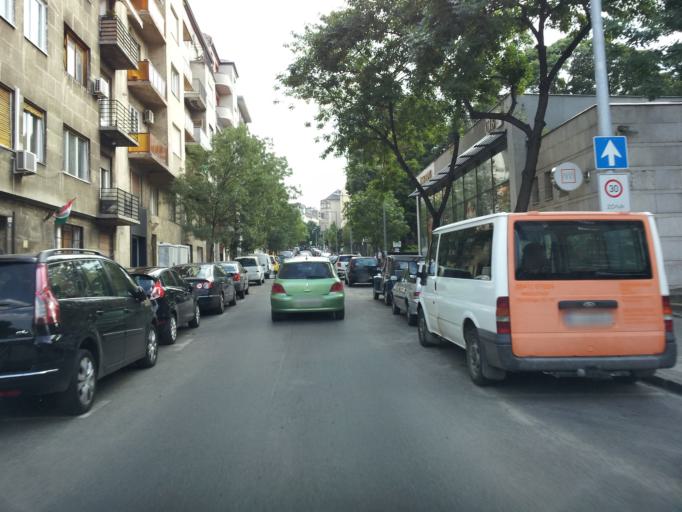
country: HU
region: Budapest
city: Budapest XII. keruelet
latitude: 47.5016
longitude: 19.0233
